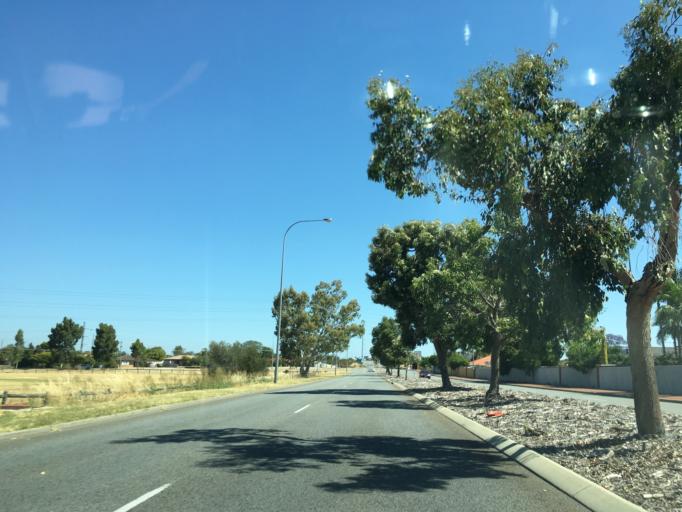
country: AU
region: Western Australia
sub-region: Canning
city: Canning Vale
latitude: -32.0519
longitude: 115.9044
